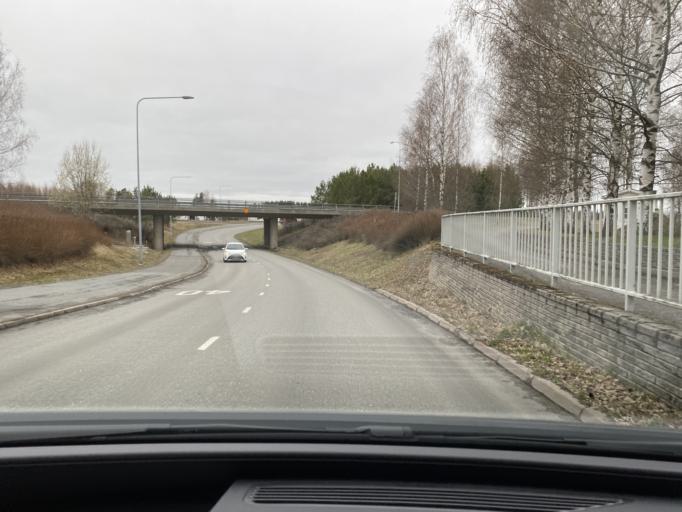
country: FI
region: Satakunta
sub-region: Pori
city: Huittinen
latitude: 61.1823
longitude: 22.6851
